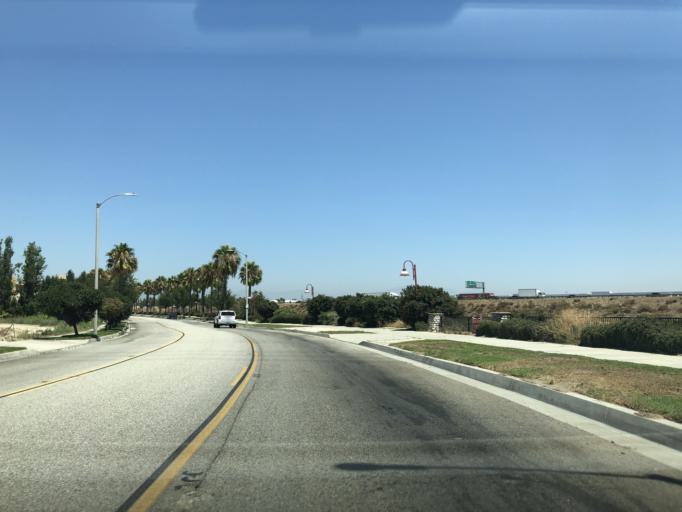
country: US
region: California
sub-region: San Bernardino County
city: Rancho Cucamonga
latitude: 34.1011
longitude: -117.5411
